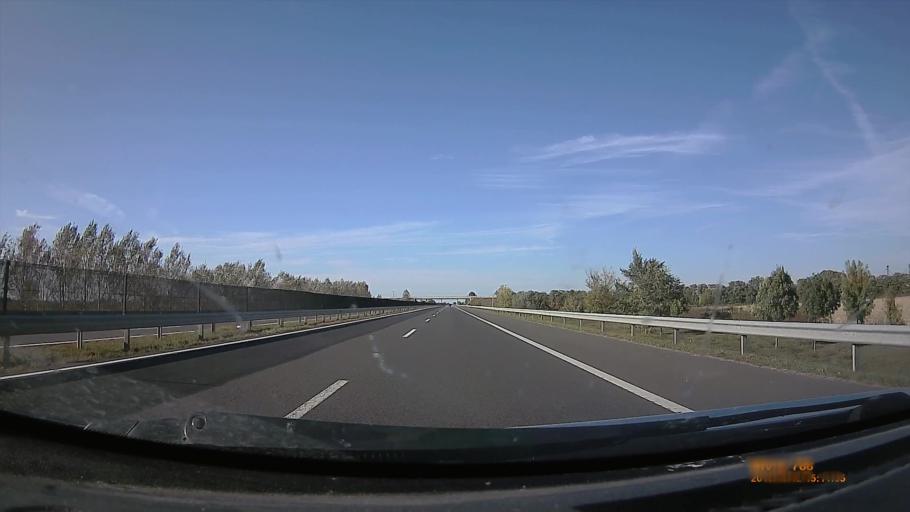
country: HU
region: Hajdu-Bihar
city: Hajduboszormeny
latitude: 47.6810
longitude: 21.4545
